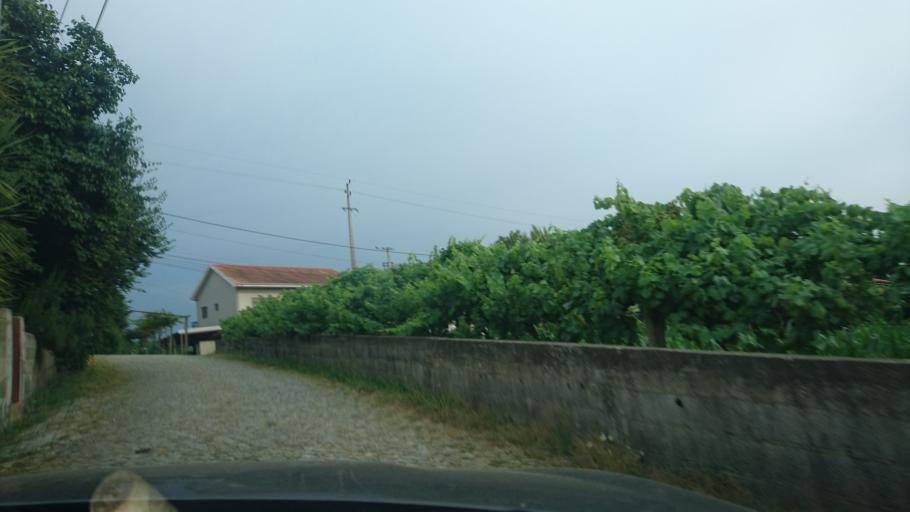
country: PT
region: Porto
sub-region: Paredes
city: Recarei
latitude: 41.1565
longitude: -8.4007
